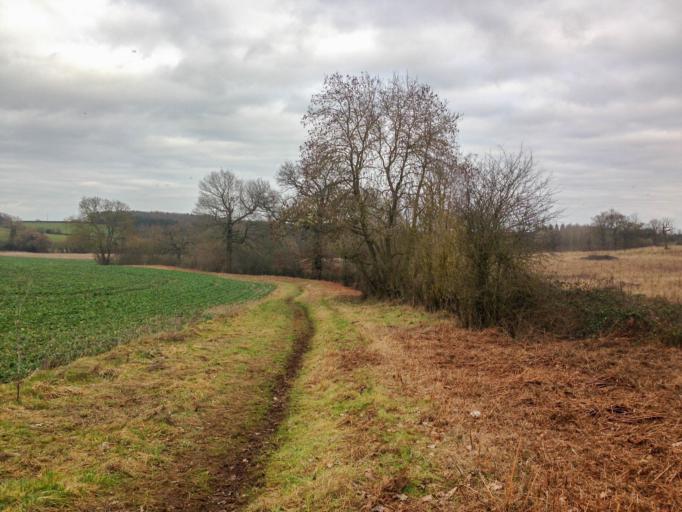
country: GB
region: England
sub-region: Warwickshire
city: Wroxall
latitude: 52.3490
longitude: -1.6410
